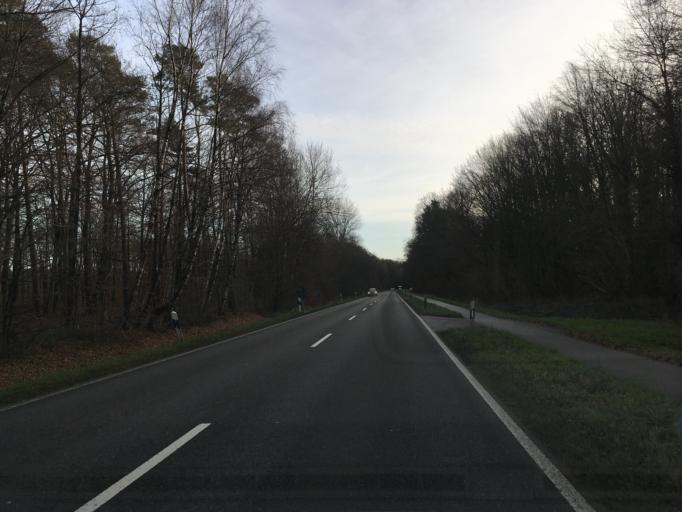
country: DE
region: North Rhine-Westphalia
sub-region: Regierungsbezirk Munster
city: Ahaus
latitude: 52.0429
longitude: 7.0188
